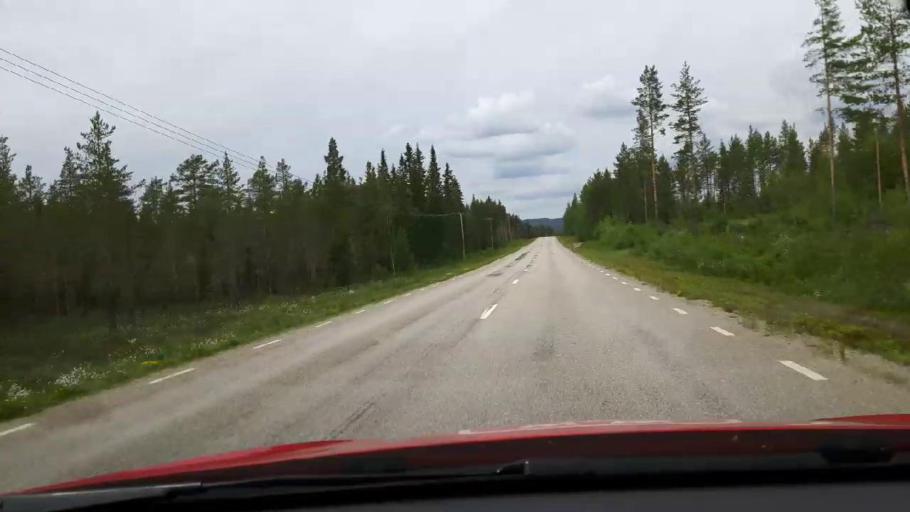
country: SE
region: Jaemtland
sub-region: Harjedalens Kommun
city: Sveg
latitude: 62.3946
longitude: 13.7531
